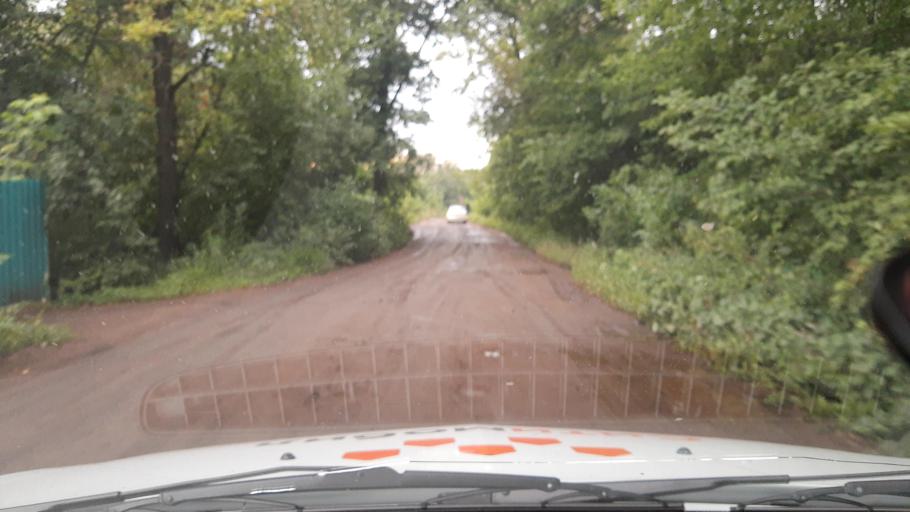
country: RU
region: Bashkortostan
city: Ufa
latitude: 54.5674
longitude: 55.9521
